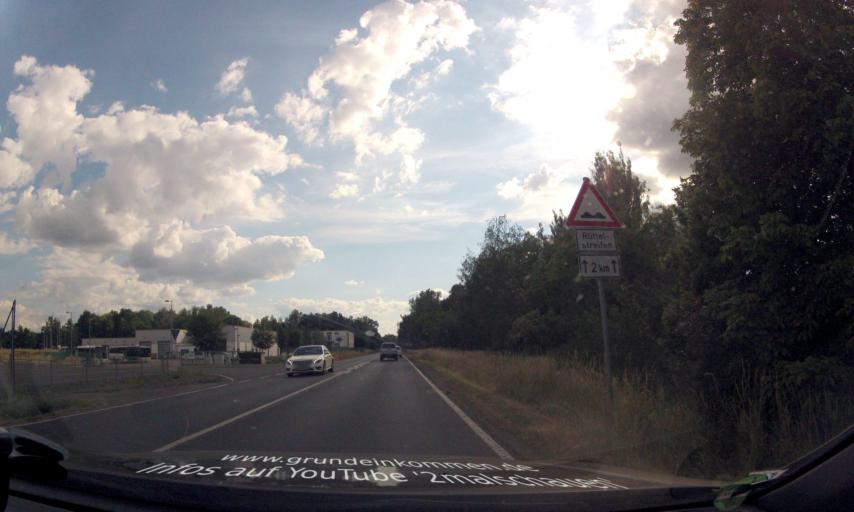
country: DE
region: Saxony
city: Bennewitz
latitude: 51.3614
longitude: 12.6937
